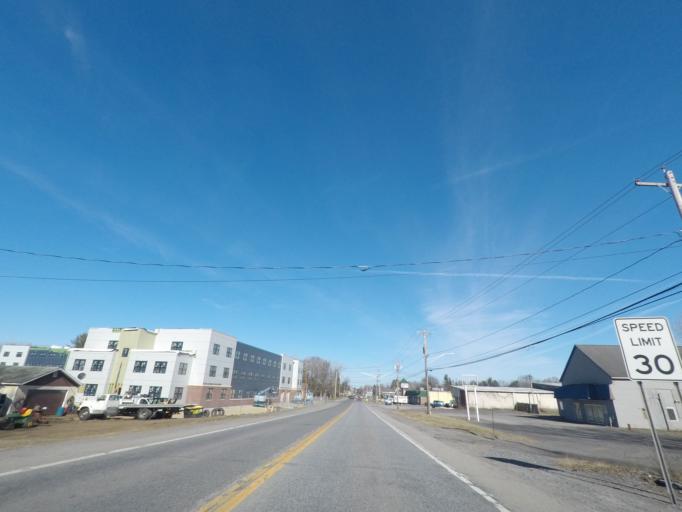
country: US
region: New York
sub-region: Saratoga County
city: Saratoga Springs
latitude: 43.0791
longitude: -73.8079
